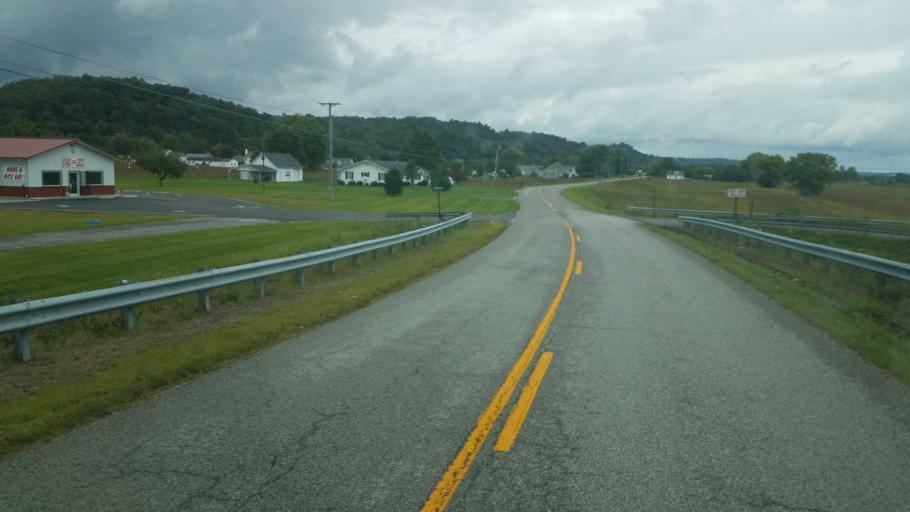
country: US
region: Ohio
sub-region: Scioto County
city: Franklin Furnace
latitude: 38.6473
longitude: -82.8731
